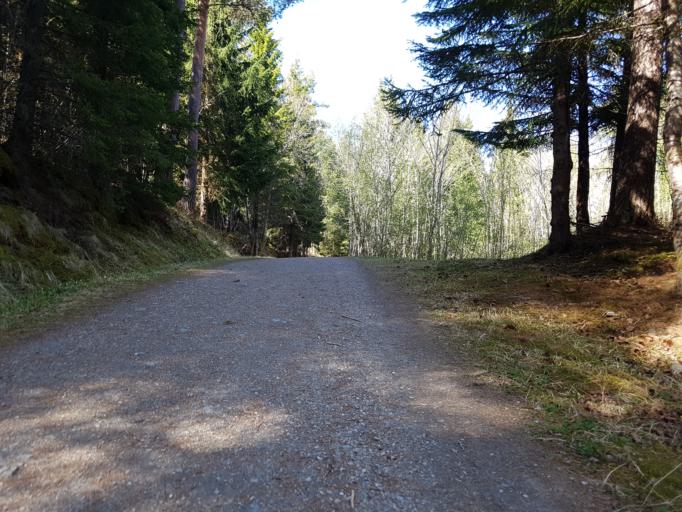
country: NO
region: Sor-Trondelag
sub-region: Trondheim
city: Trondheim
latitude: 63.4329
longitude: 10.3461
